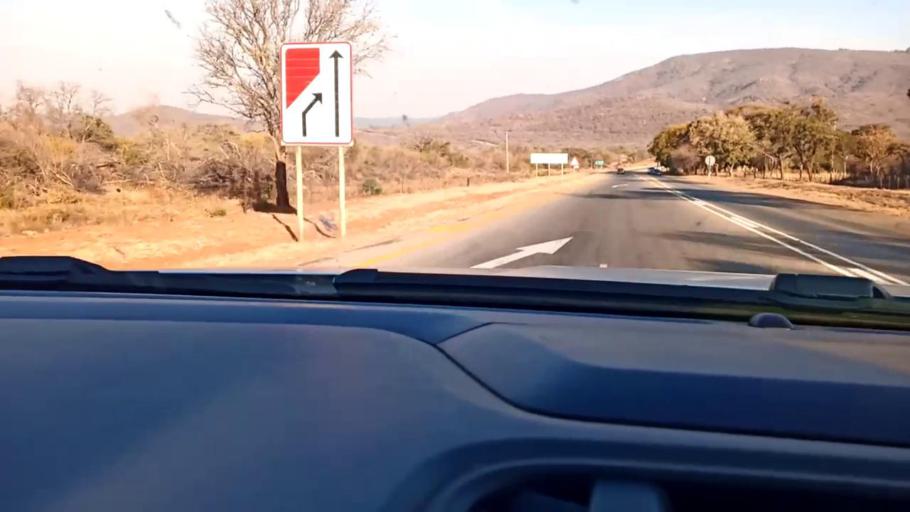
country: ZA
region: Limpopo
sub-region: Mopani District Municipality
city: Duiwelskloof
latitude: -23.6226
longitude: 30.1278
